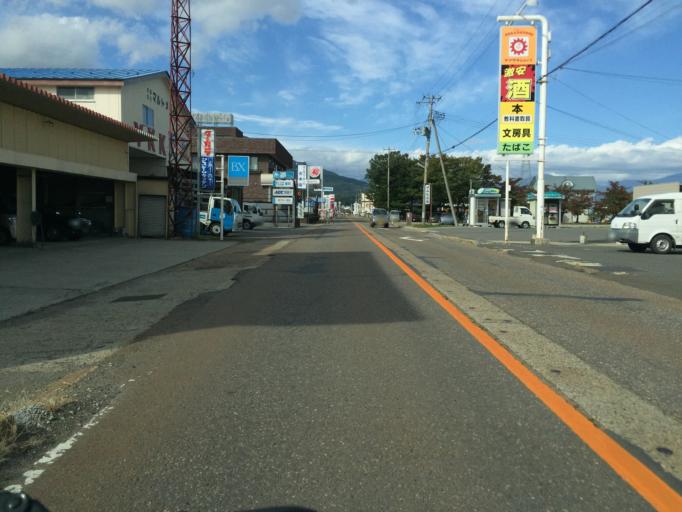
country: JP
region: Fukushima
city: Inawashiro
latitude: 37.5493
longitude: 140.1059
